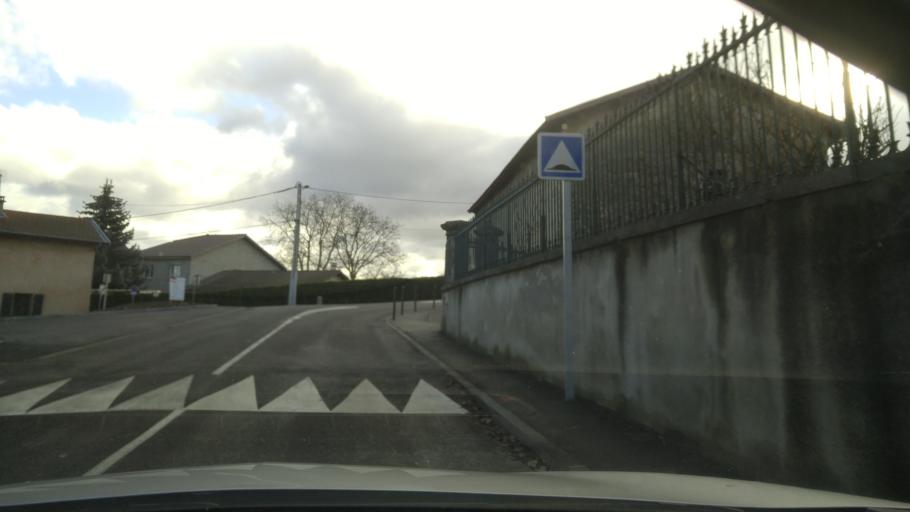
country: FR
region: Rhone-Alpes
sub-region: Departement de l'Isere
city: Roche
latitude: 45.5904
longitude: 5.1613
